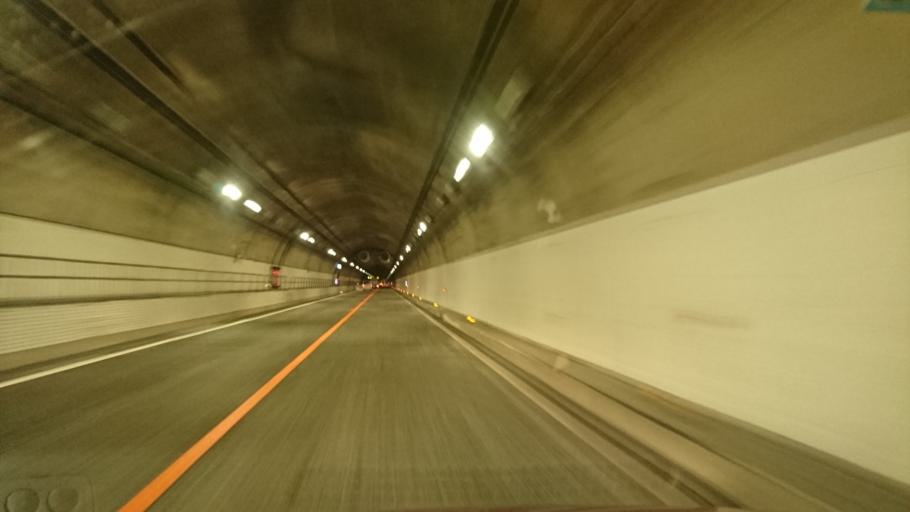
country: JP
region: Okayama
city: Okayama-shi
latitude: 34.7199
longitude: 133.9473
